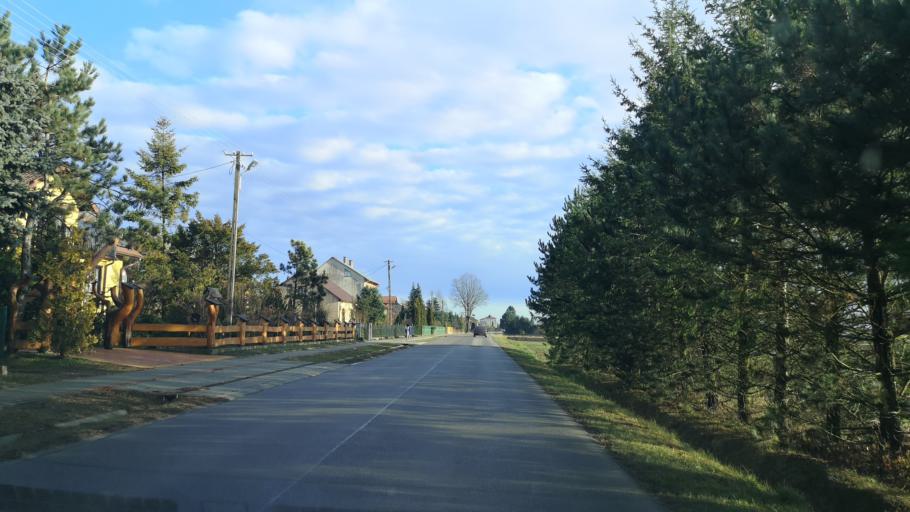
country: PL
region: Subcarpathian Voivodeship
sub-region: Powiat lezajski
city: Piskorowice
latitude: 50.2440
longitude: 22.5105
